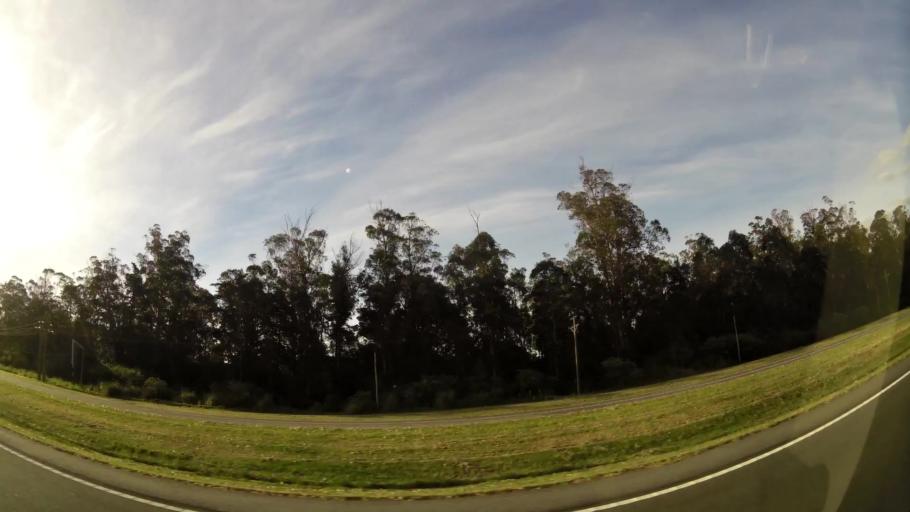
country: UY
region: Maldonado
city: Piriapolis
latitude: -34.7847
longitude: -55.3665
